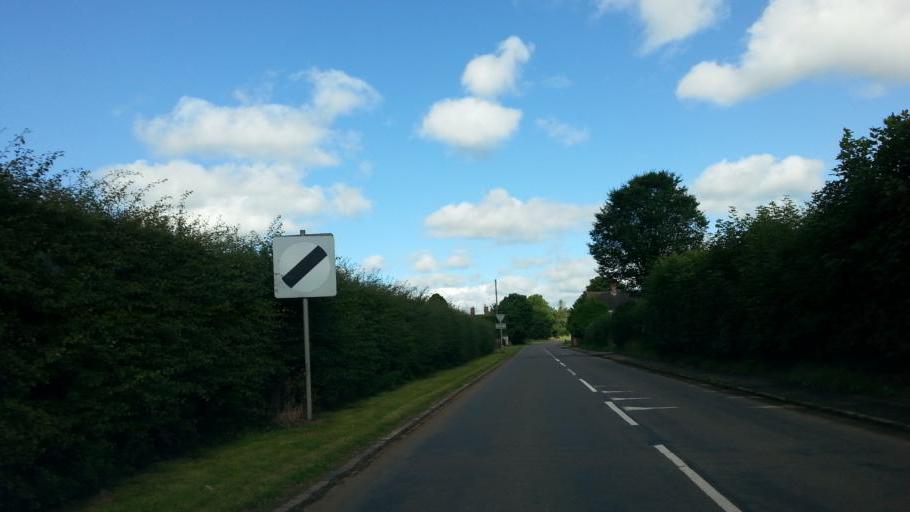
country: GB
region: England
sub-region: Staffordshire
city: Rugeley
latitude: 52.8216
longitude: -1.8907
